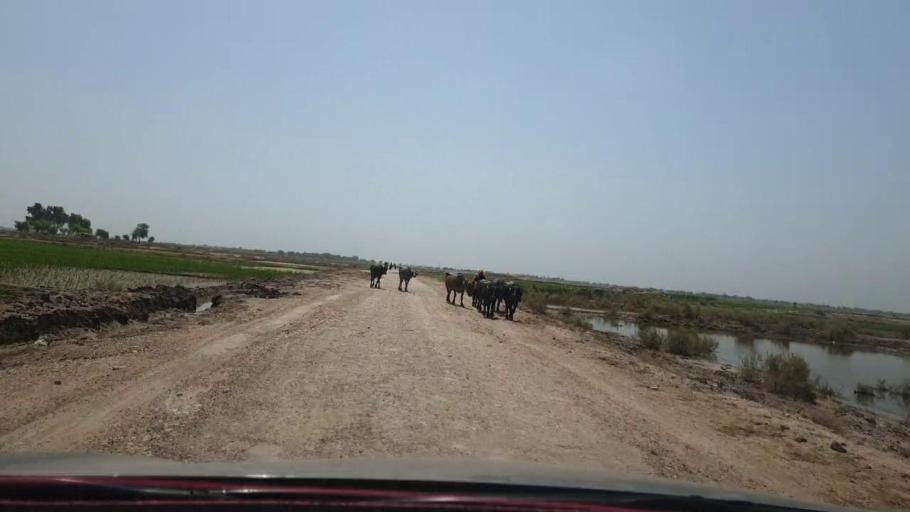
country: PK
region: Sindh
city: Kambar
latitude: 27.5824
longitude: 67.8771
